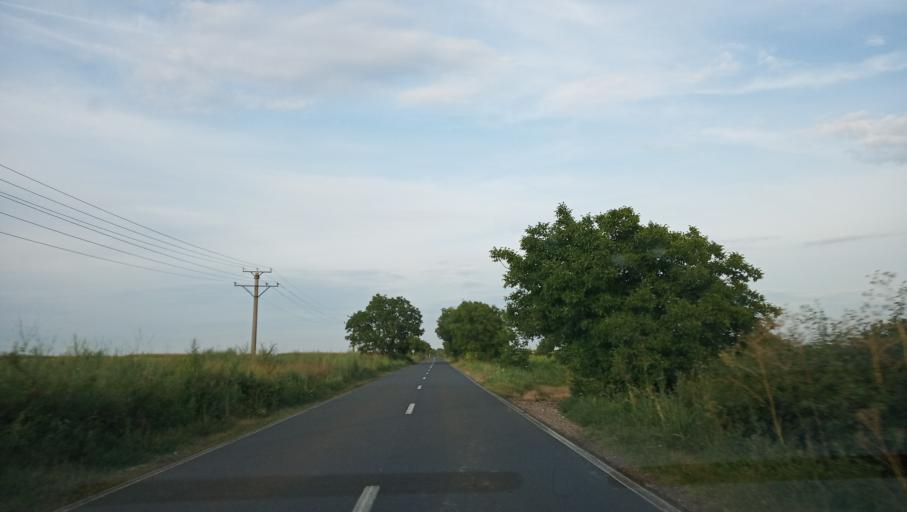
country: RO
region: Giurgiu
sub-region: Comuna Prundu
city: Prundu
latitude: 44.0999
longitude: 26.2638
